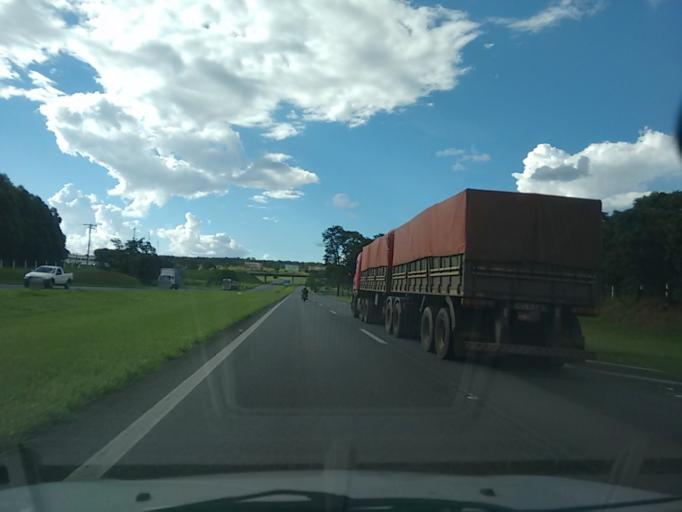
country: BR
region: Sao Paulo
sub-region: Sao Carlos
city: Sao Carlos
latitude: -22.0487
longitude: -47.8594
